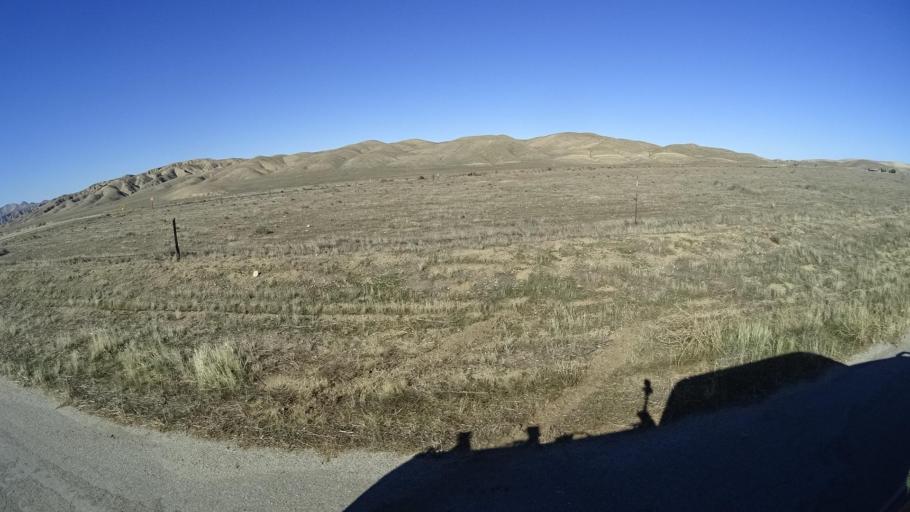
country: US
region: California
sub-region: Kern County
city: Maricopa
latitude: 34.9379
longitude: -119.4669
